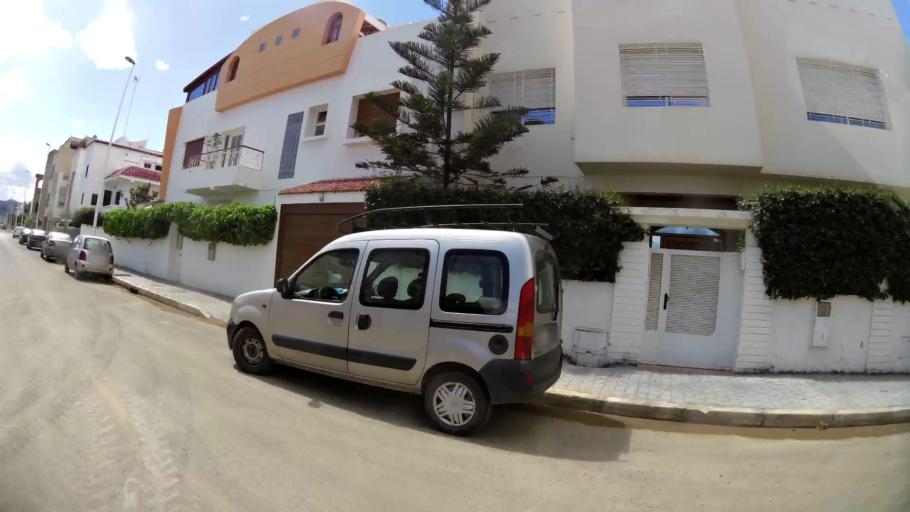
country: MA
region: Tanger-Tetouan
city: Tetouan
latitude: 35.5819
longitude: -5.3338
